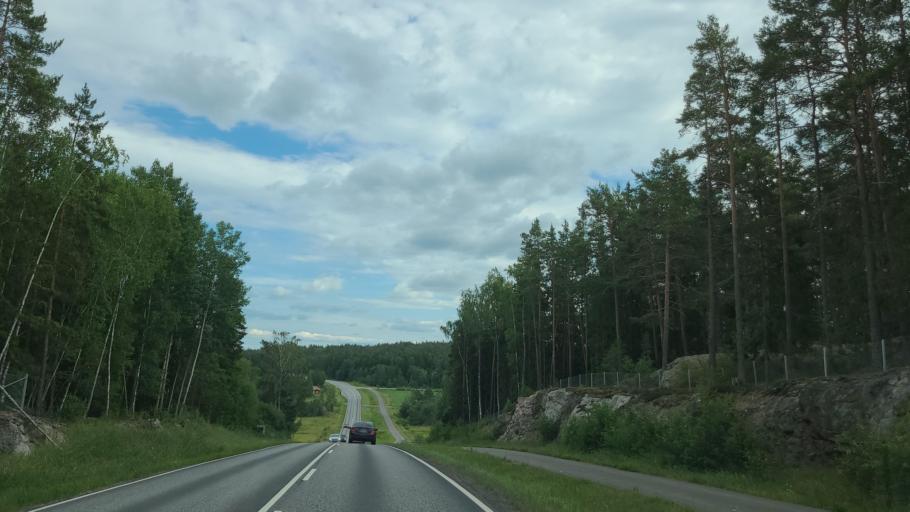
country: FI
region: Varsinais-Suomi
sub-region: Turku
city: Rymaettylae
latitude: 60.3952
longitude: 21.9013
